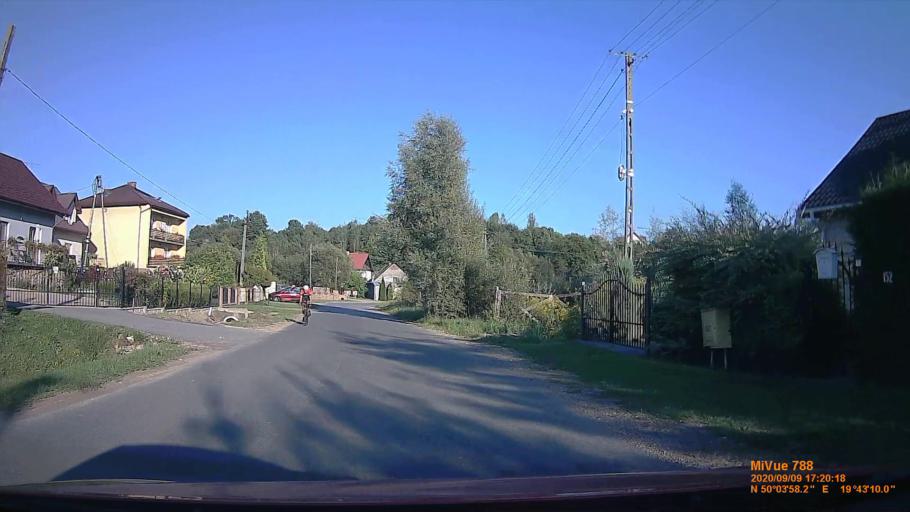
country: PL
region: Lesser Poland Voivodeship
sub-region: Powiat krakowski
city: Mnikow
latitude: 50.0661
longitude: 19.7196
